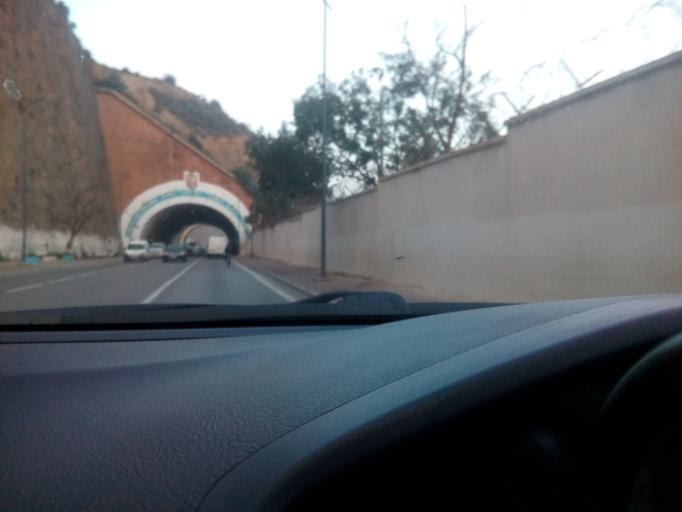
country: DZ
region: Oran
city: Oran
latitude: 35.7124
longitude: -0.6724
